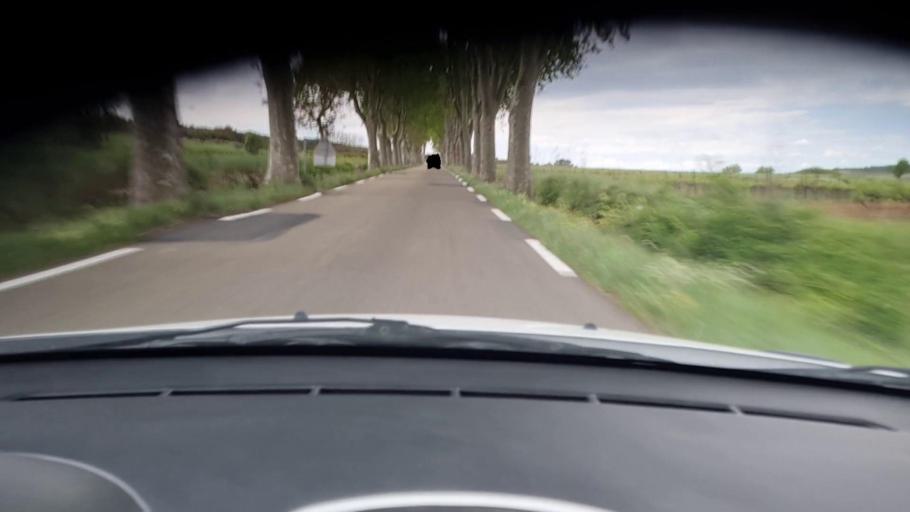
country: FR
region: Languedoc-Roussillon
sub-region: Departement du Gard
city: Uzes
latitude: 43.9795
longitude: 4.4067
